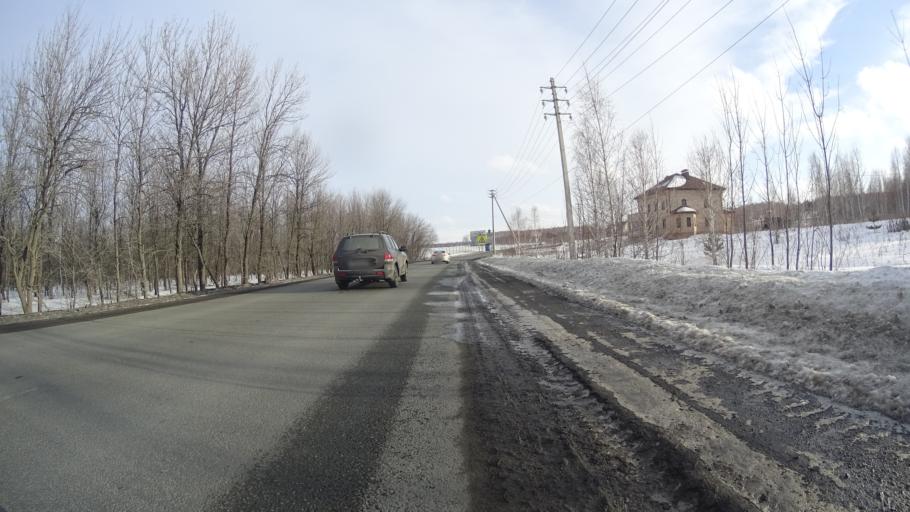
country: RU
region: Chelyabinsk
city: Sargazy
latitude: 55.1353
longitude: 61.2847
